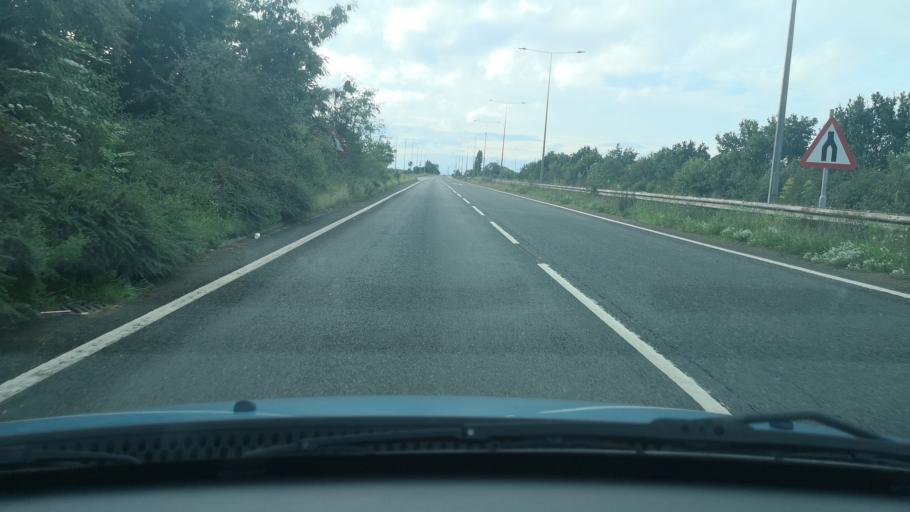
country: GB
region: England
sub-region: Doncaster
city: Marr
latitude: 53.5791
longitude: -1.2168
